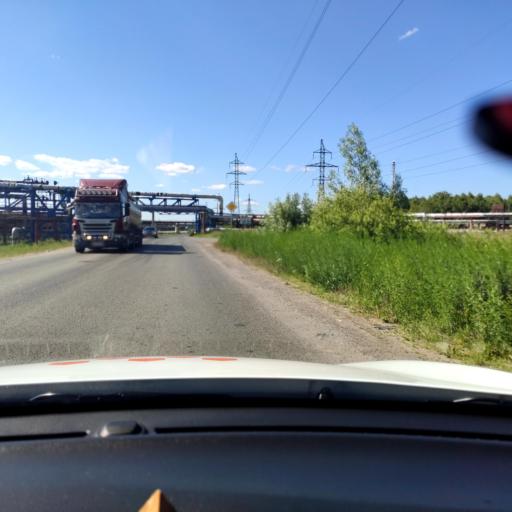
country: RU
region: Tatarstan
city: Staroye Arakchino
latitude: 55.8704
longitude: 48.9738
